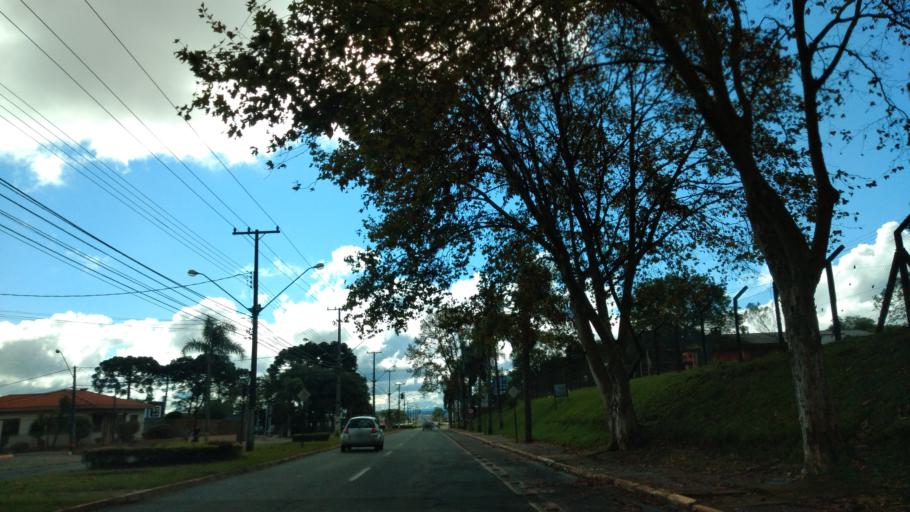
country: BR
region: Parana
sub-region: Guarapuava
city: Guarapuava
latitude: -25.3846
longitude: -51.4658
